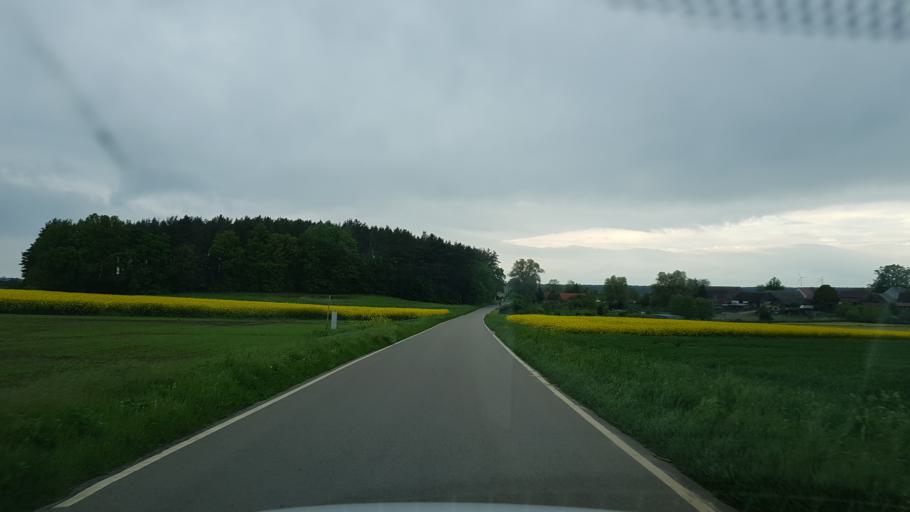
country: PL
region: West Pomeranian Voivodeship
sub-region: Powiat pyrzycki
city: Bielice
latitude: 53.1301
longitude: 14.7491
